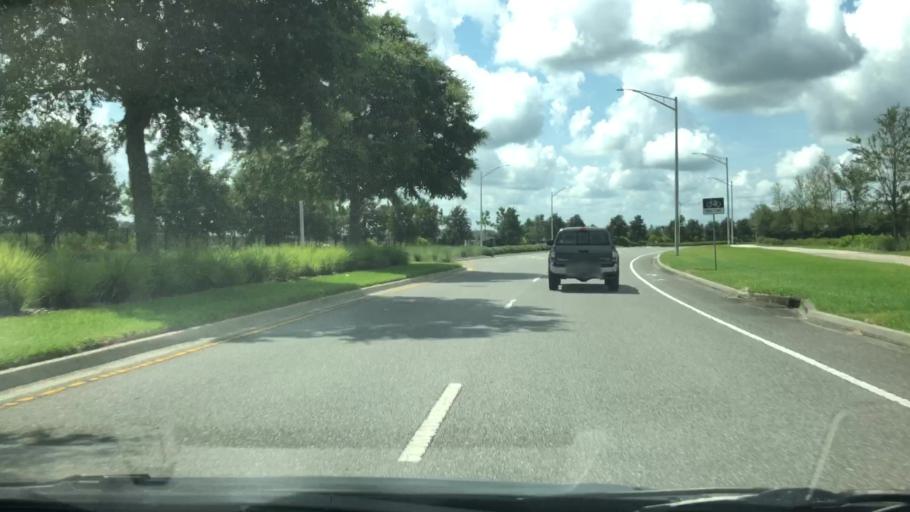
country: US
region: Florida
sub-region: Saint Johns County
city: Fruit Cove
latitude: 30.1114
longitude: -81.5180
